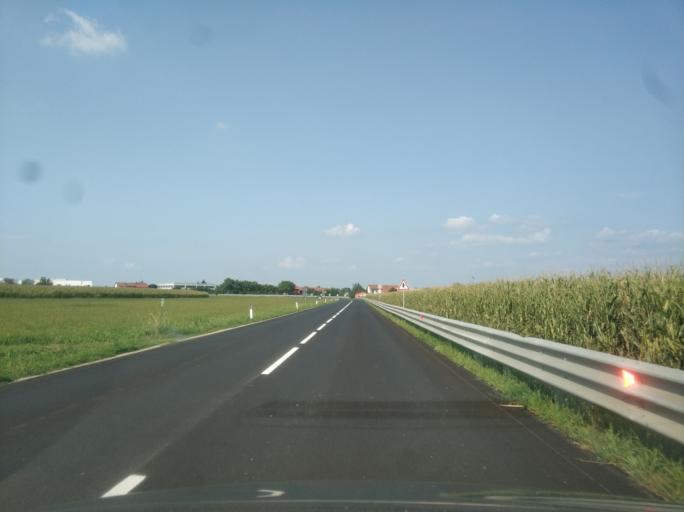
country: IT
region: Piedmont
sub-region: Provincia di Cuneo
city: Cervere
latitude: 44.6236
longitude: 7.7820
